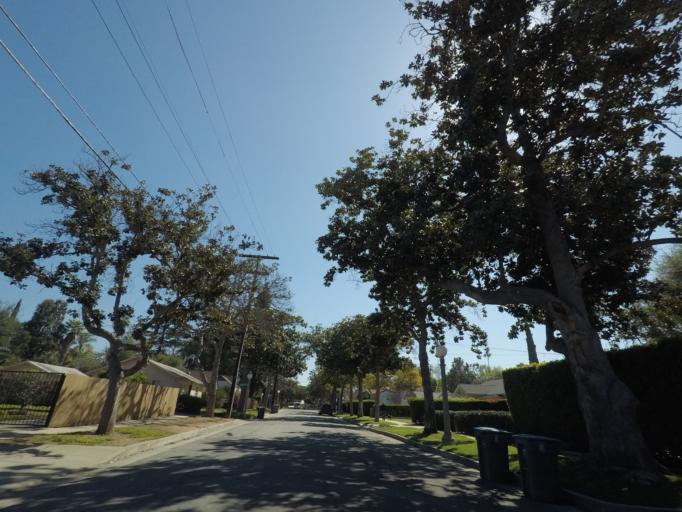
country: US
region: California
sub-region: Los Angeles County
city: South Pasadena
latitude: 34.1294
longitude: -118.1424
